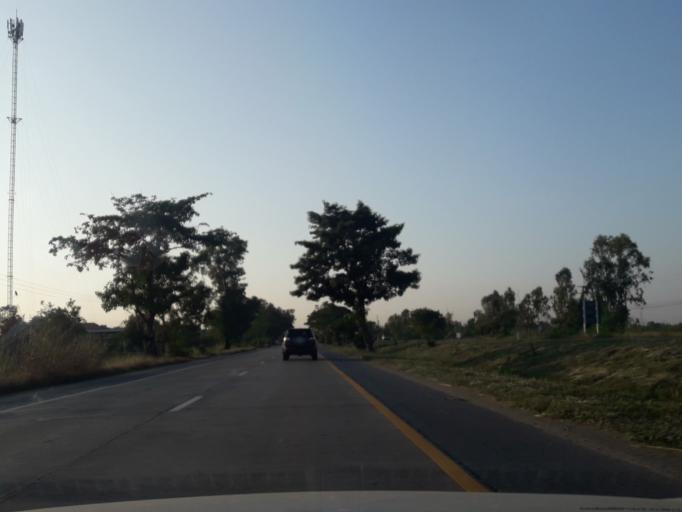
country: TH
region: Phra Nakhon Si Ayutthaya
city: Bang Pa-in
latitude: 14.2883
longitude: 100.5254
